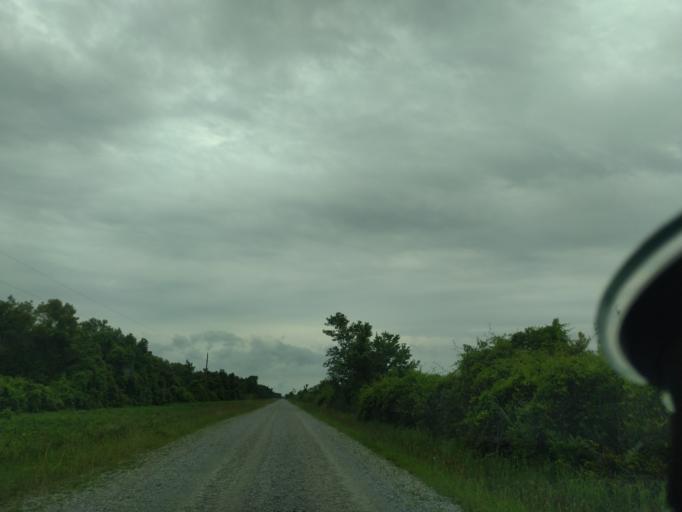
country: US
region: North Carolina
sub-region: Beaufort County
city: Belhaven
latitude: 35.7431
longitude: -76.4854
